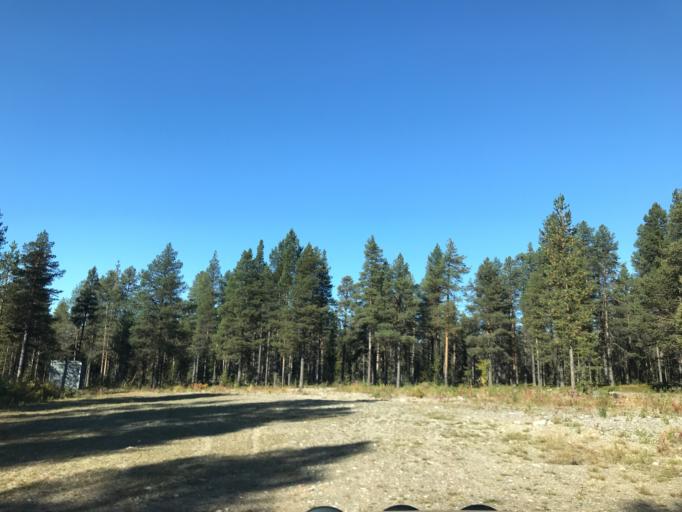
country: SE
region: Norrbotten
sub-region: Gallivare Kommun
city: Malmberget
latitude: 67.6496
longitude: 21.0819
